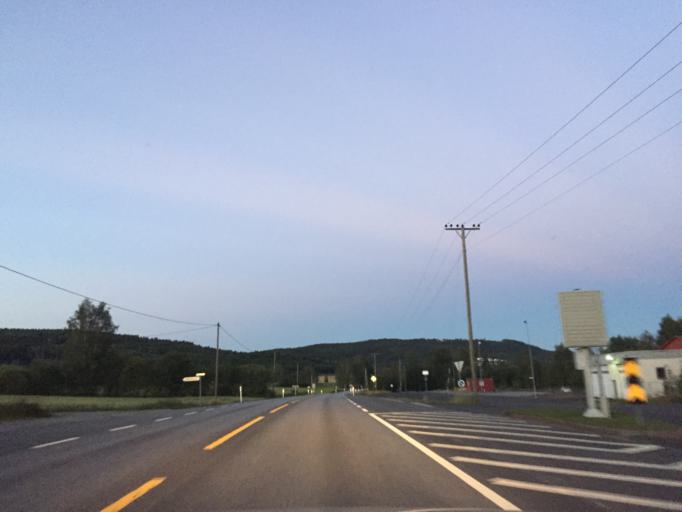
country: NO
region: Hedmark
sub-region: Kongsvinger
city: Spetalen
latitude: 60.2149
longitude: 11.9304
